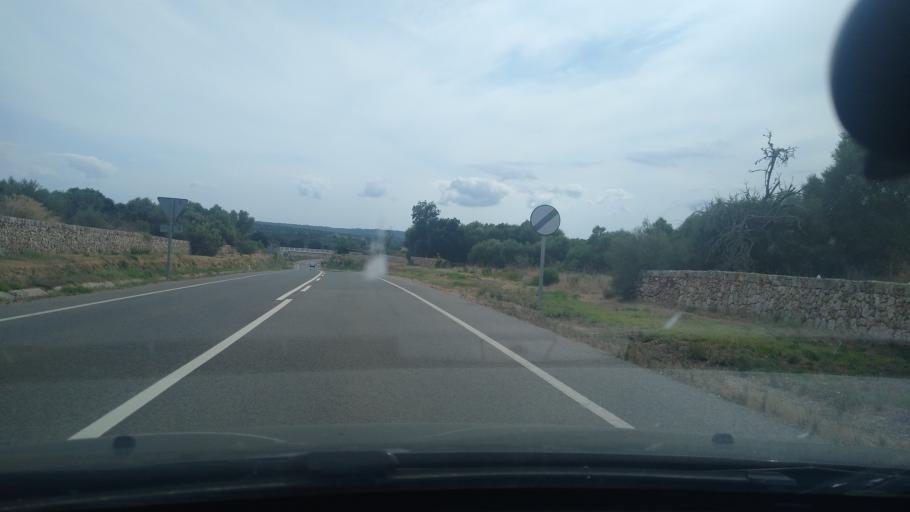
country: ES
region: Balearic Islands
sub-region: Illes Balears
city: Llubi
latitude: 39.6999
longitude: 3.0148
